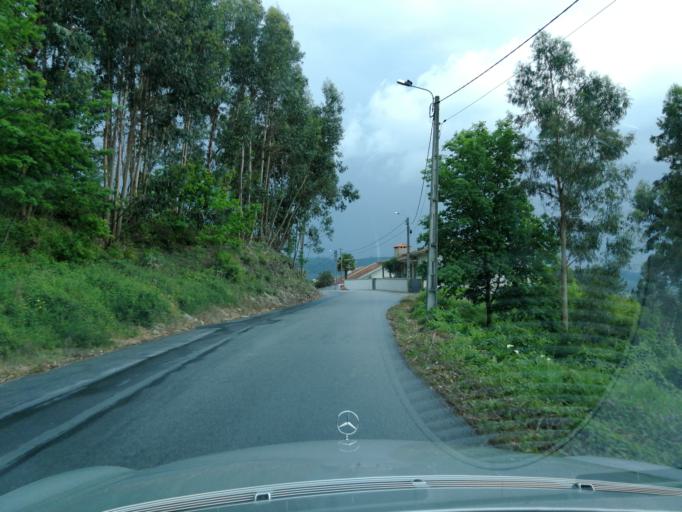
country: PT
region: Braga
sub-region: Braga
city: Oliveira
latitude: 41.4551
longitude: -8.4771
